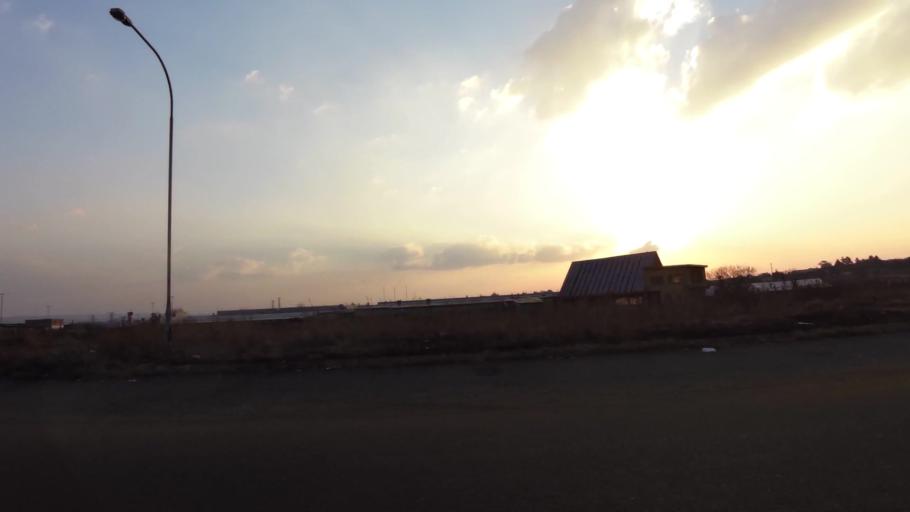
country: ZA
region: Gauteng
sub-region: City of Johannesburg Metropolitan Municipality
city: Soweto
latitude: -26.2916
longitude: 27.9085
